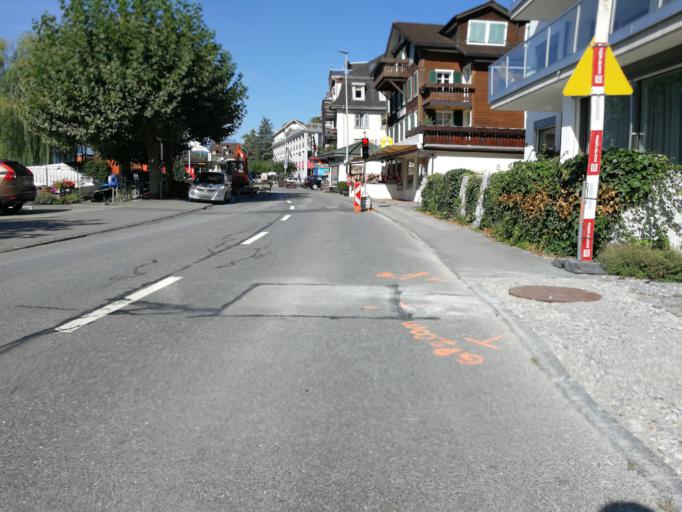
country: CH
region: Schwyz
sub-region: Bezirk Gersau
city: Gersau
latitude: 46.9909
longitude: 8.5279
